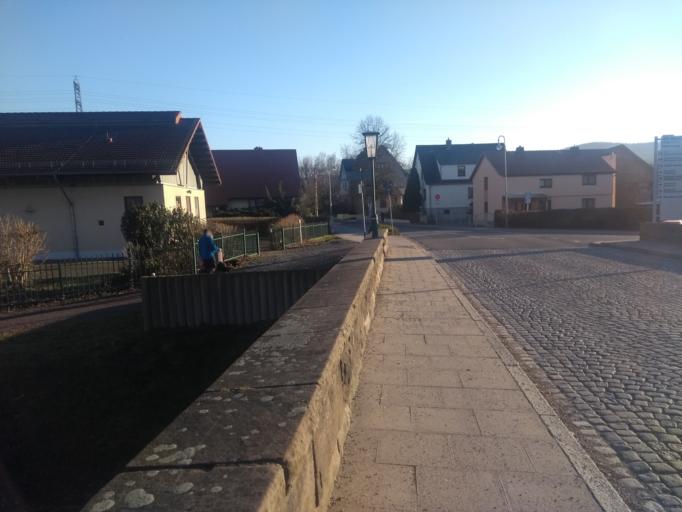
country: DE
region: Thuringia
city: Breitungen
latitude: 50.7611
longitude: 10.3266
